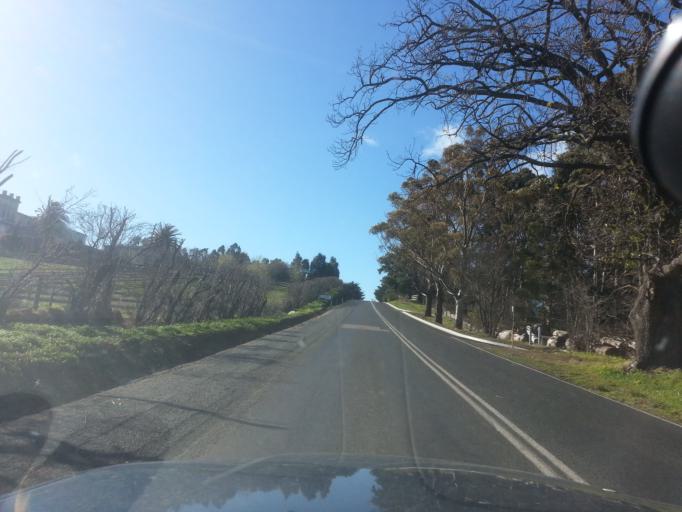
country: AU
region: Victoria
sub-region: Casey
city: Narre Warren North
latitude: -37.9993
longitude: 145.3328
